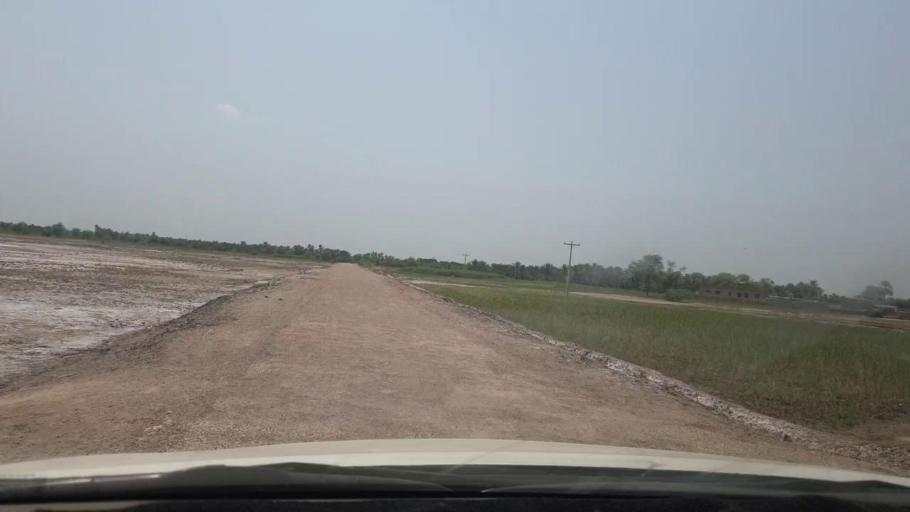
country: PK
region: Sindh
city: Khairpur
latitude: 27.5123
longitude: 68.8177
